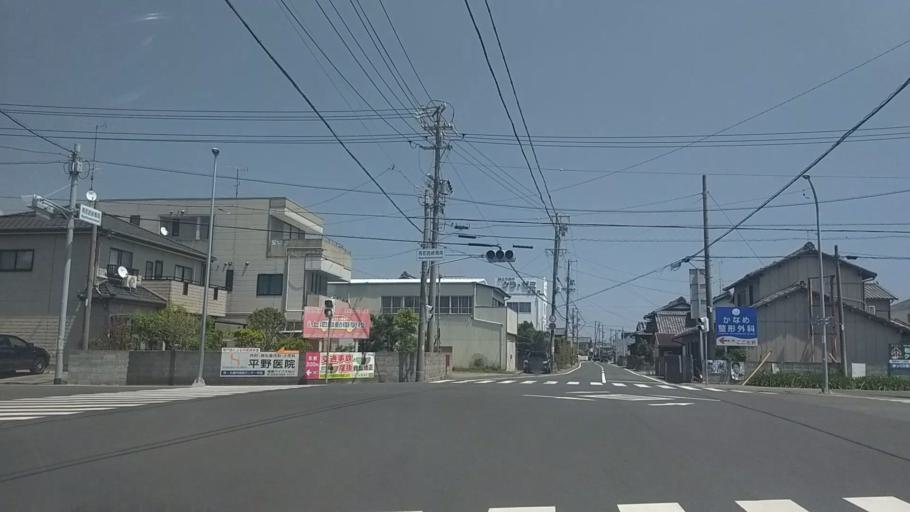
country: JP
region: Shizuoka
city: Kosai-shi
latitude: 34.6837
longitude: 137.6301
